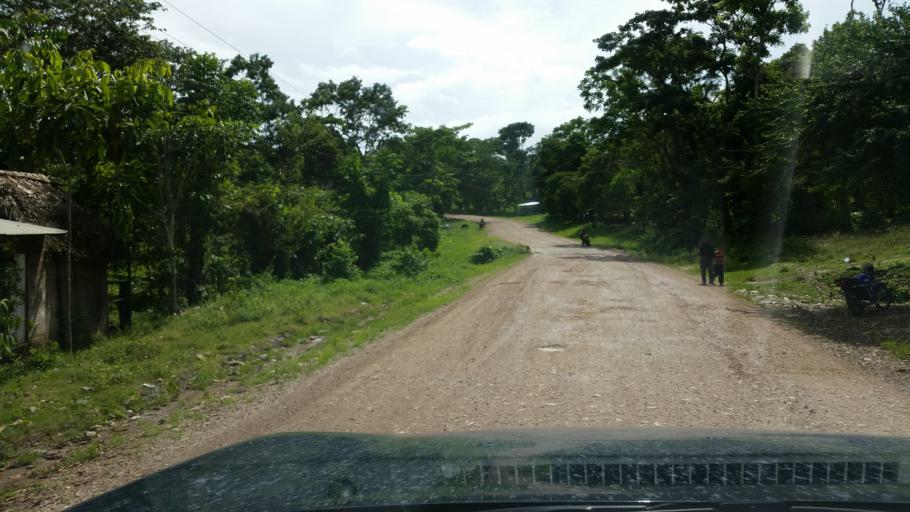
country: NI
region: Atlantico Norte (RAAN)
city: Siuna
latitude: 13.6813
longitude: -84.6501
